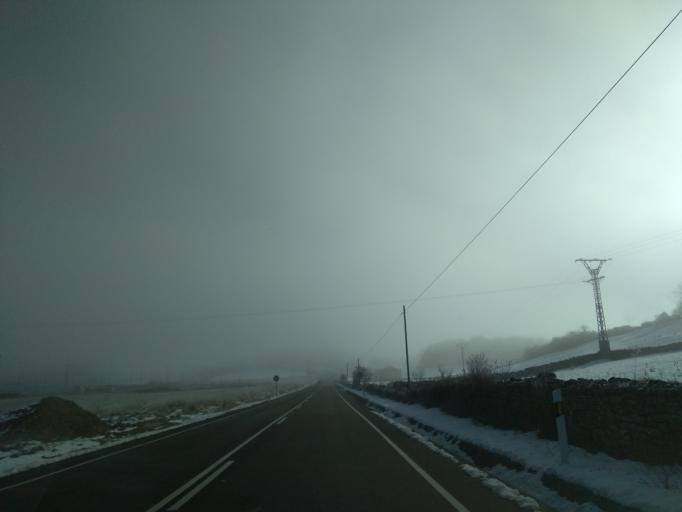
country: ES
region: Castille and Leon
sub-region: Provincia de Burgos
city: Espinosa de los Monteros
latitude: 43.0721
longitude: -3.5309
